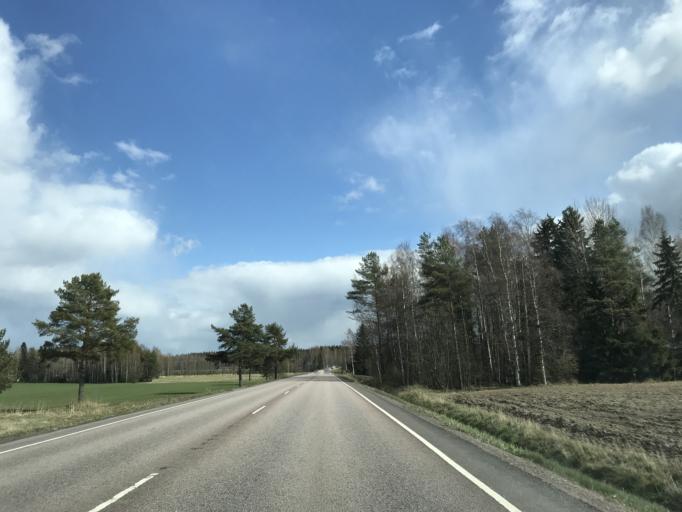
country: FI
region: Uusimaa
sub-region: Helsinki
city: Hyvinge
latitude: 60.5378
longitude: 24.9040
